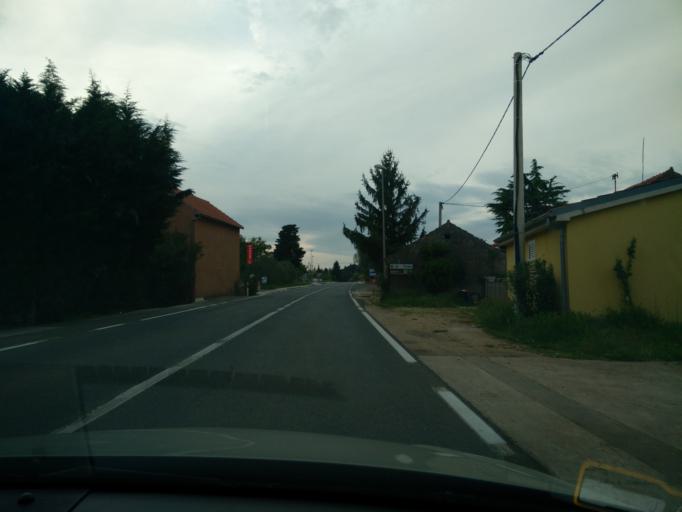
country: HR
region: Zadarska
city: Turanj
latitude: 43.9686
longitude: 15.4094
